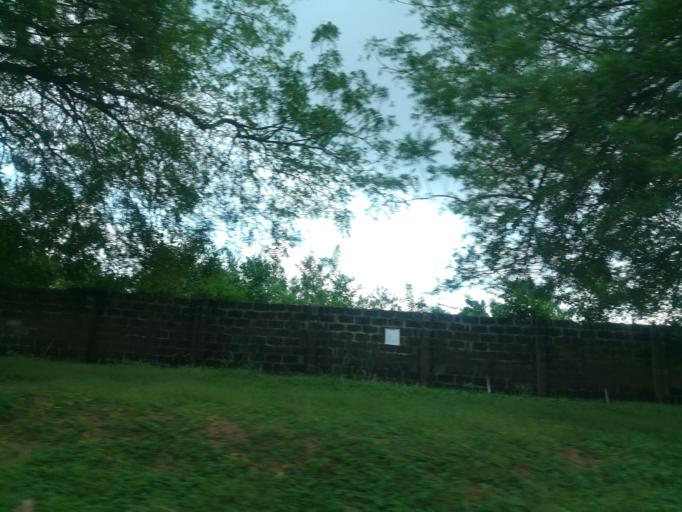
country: NG
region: Oyo
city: Ibadan
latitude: 7.4330
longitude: 3.8900
